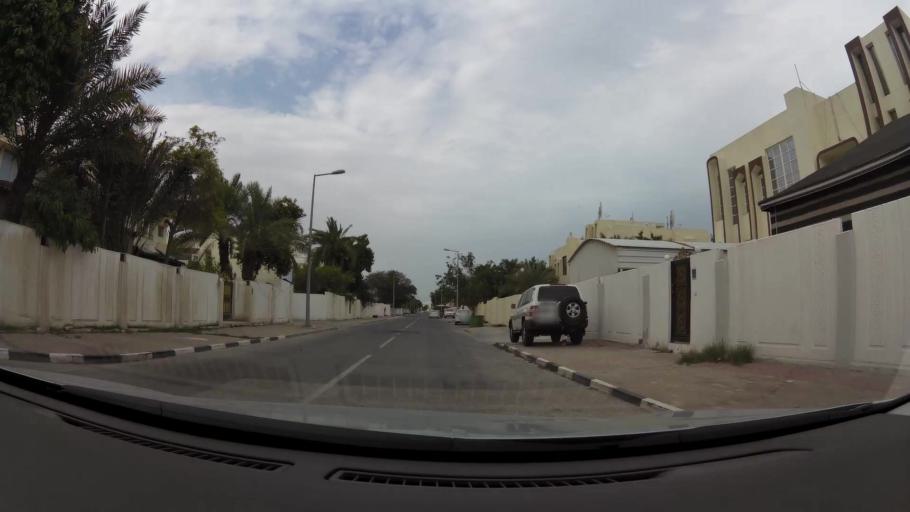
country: QA
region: Baladiyat ad Dawhah
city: Doha
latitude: 25.3309
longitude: 51.5053
